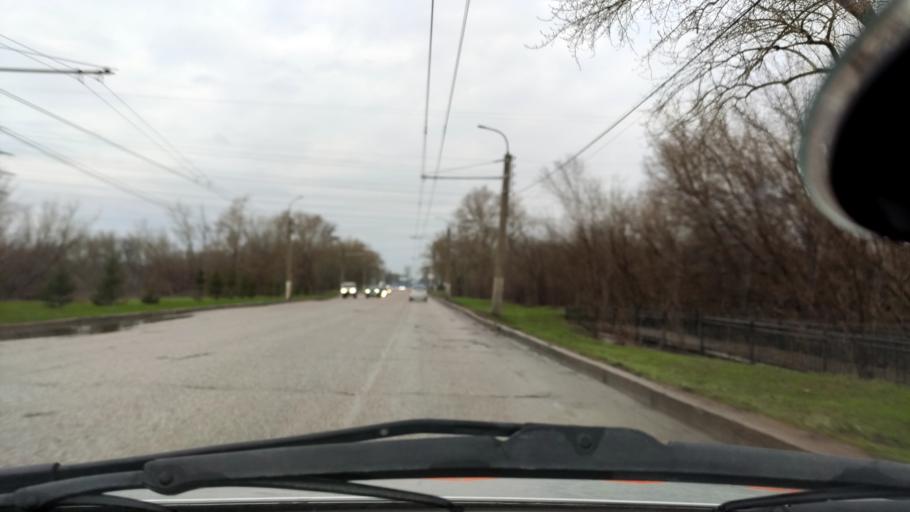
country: RU
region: Bashkortostan
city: Sterlitamak
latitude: 53.6596
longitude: 55.9489
